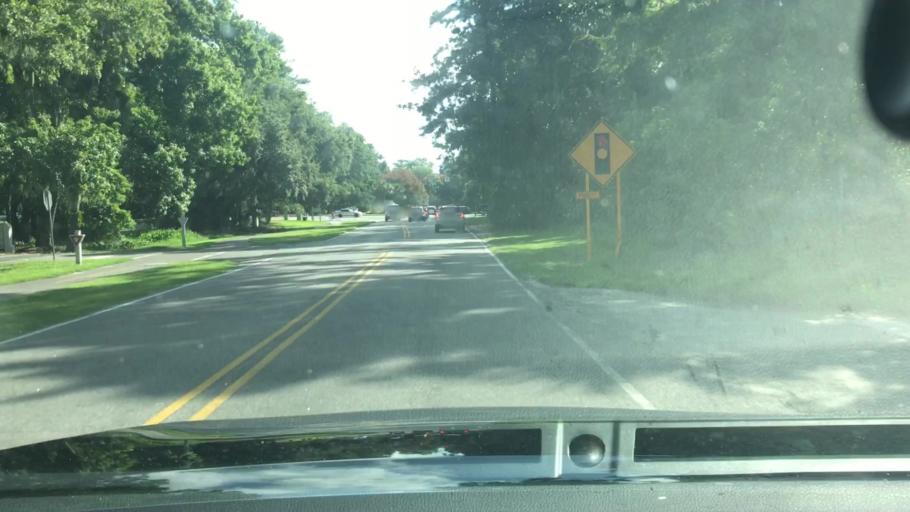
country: US
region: South Carolina
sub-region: Beaufort County
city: Hilton Head Island
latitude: 32.1469
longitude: -80.7575
